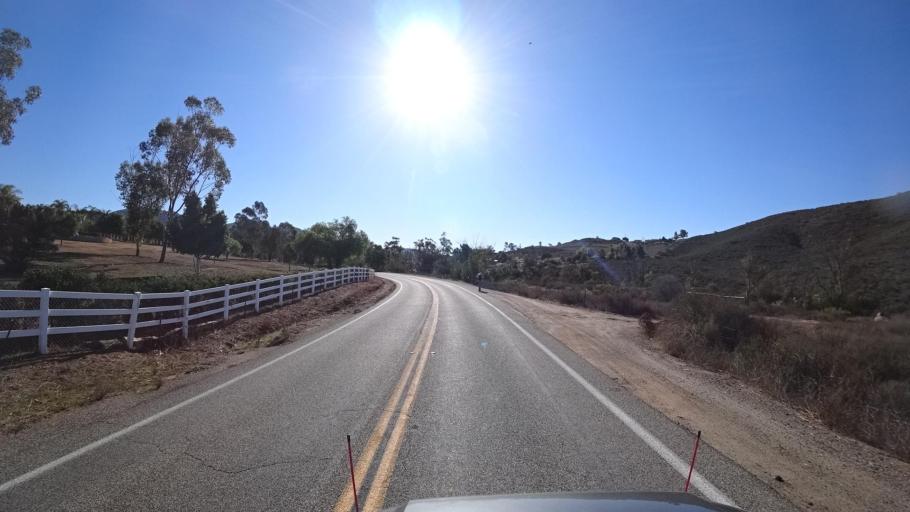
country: US
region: California
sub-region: San Diego County
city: Jamul
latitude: 32.6661
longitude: -116.7972
